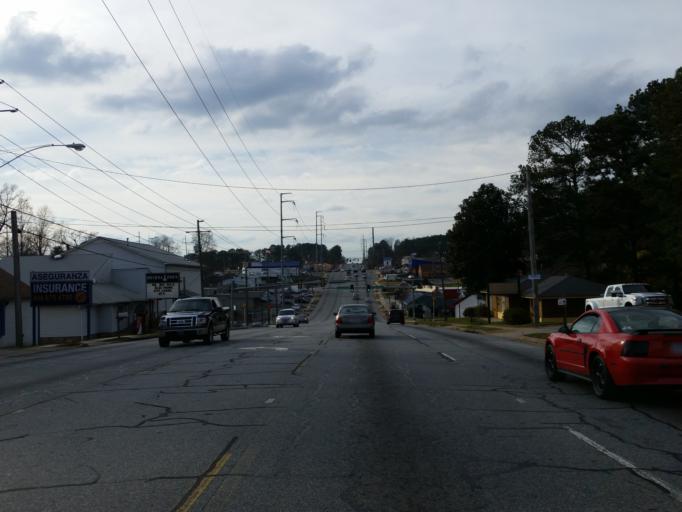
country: US
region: Georgia
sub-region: Cobb County
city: Smyrna
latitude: 33.8945
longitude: -84.5341
